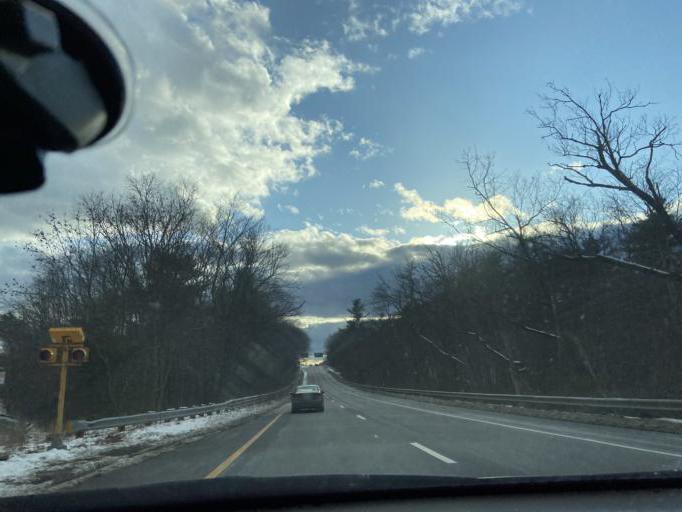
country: US
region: Massachusetts
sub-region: Norfolk County
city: Walpole
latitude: 42.1287
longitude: -71.2271
